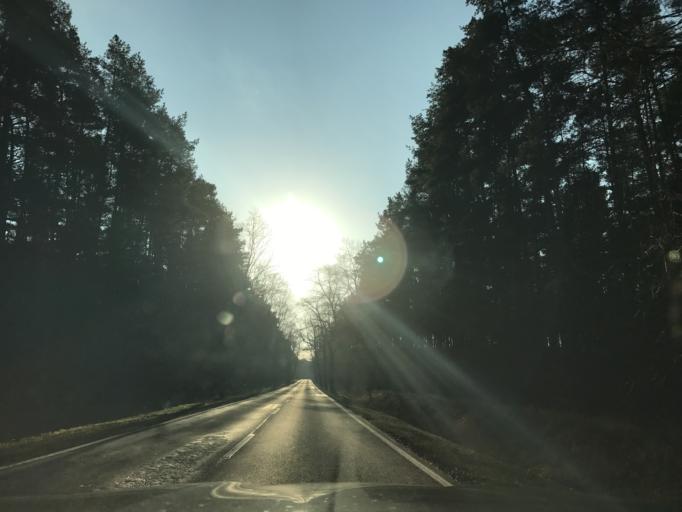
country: DE
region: Brandenburg
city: Wenzlow
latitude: 52.3420
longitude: 12.4985
